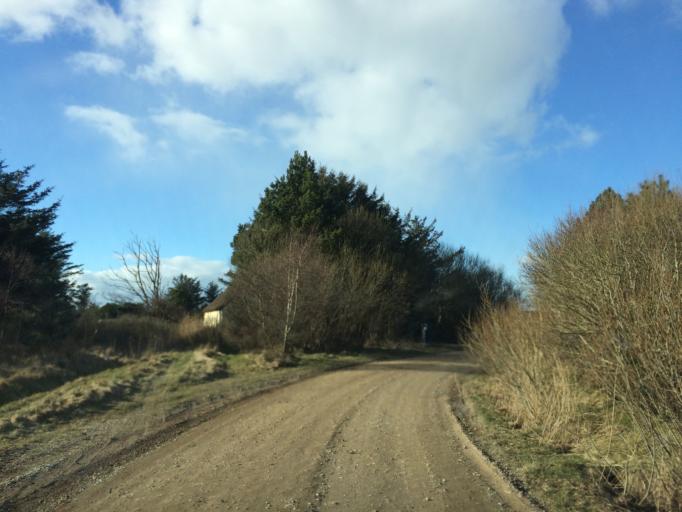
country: DK
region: Central Jutland
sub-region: Holstebro Kommune
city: Ulfborg
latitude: 56.2658
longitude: 8.1446
